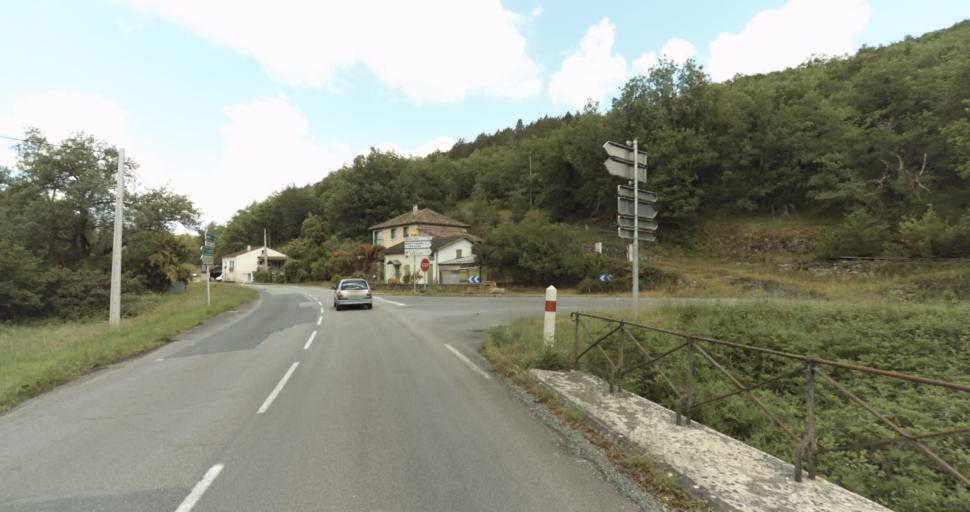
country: FR
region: Aquitaine
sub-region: Departement de la Dordogne
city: Beaumont-du-Perigord
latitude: 44.7868
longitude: 0.7643
